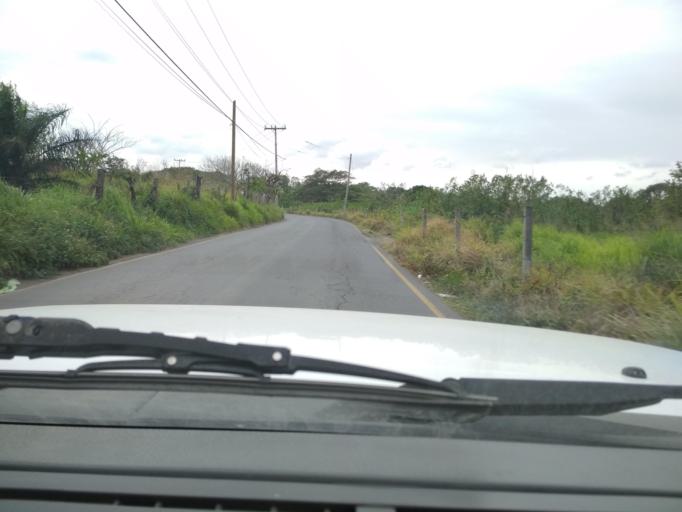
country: MX
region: Veracruz
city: Boca del Rio
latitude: 19.0901
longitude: -96.1245
